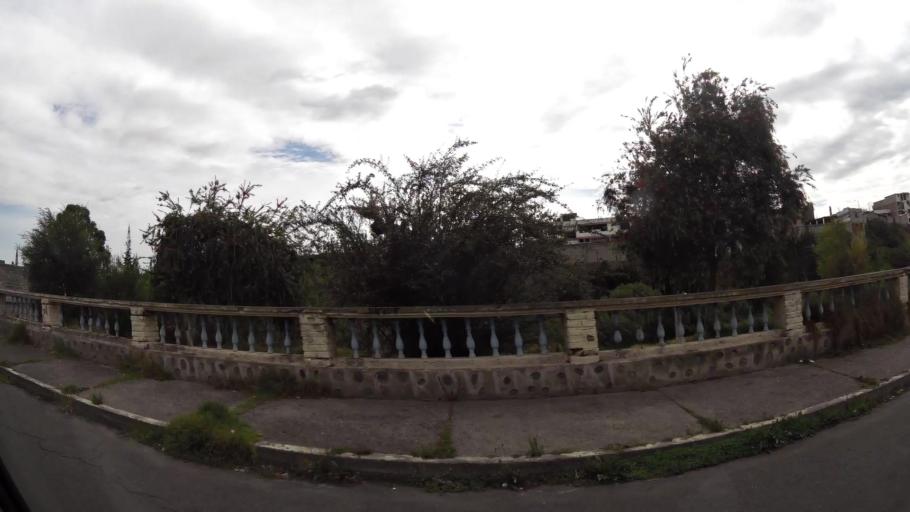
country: EC
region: Cotopaxi
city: Latacunga
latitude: -0.9303
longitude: -78.6214
